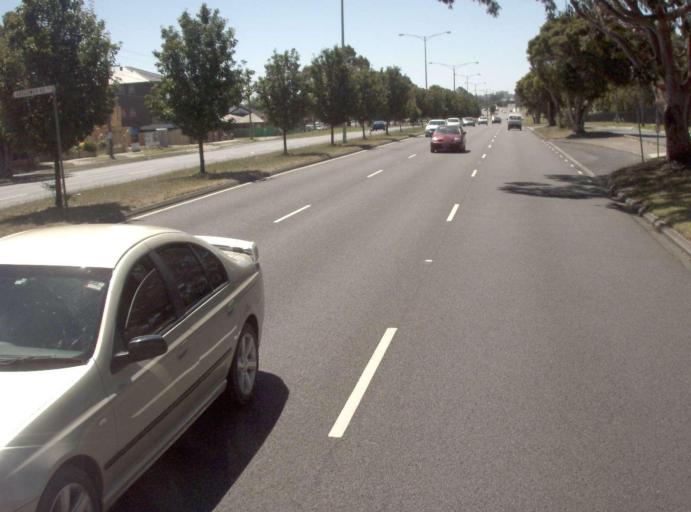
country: AU
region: Victoria
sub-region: Greater Dandenong
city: Noble Park North
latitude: -37.9515
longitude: 145.1772
